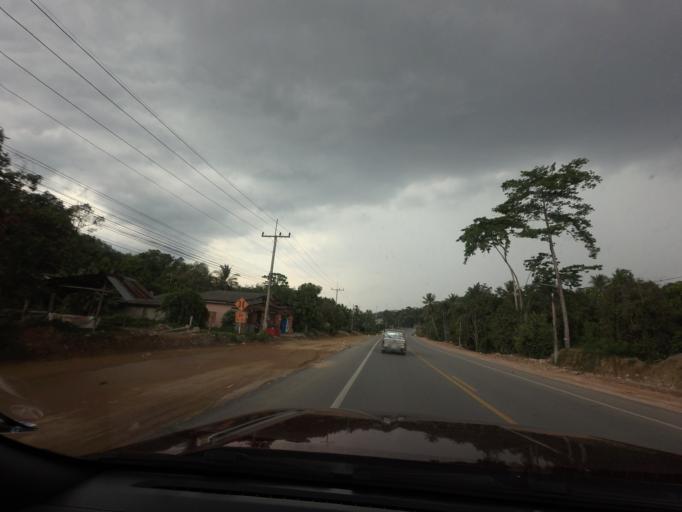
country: TH
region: Yala
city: Krong Pi Nang
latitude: 6.4046
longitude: 101.2814
